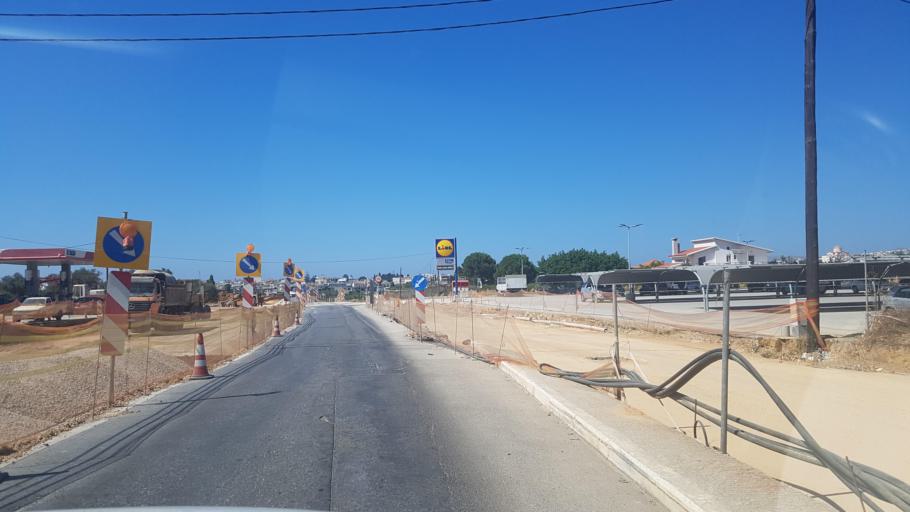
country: GR
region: Crete
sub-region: Nomos Chanias
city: Mournies
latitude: 35.4968
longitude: 24.0183
